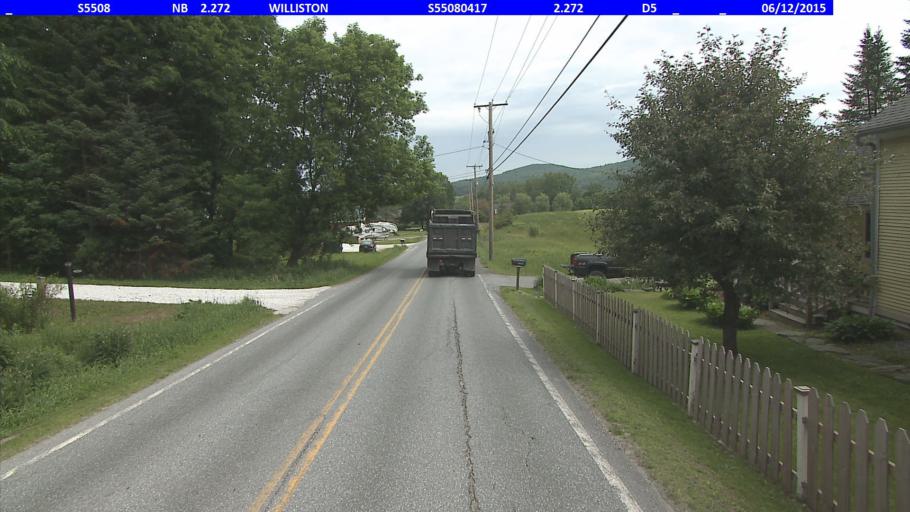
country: US
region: Vermont
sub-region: Chittenden County
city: Williston
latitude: 44.4636
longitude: -73.0488
